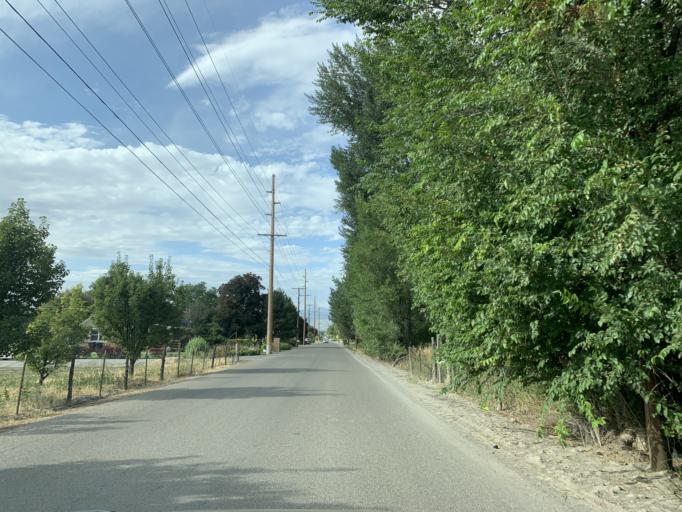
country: US
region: Utah
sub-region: Utah County
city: Provo
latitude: 40.2227
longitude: -111.6873
